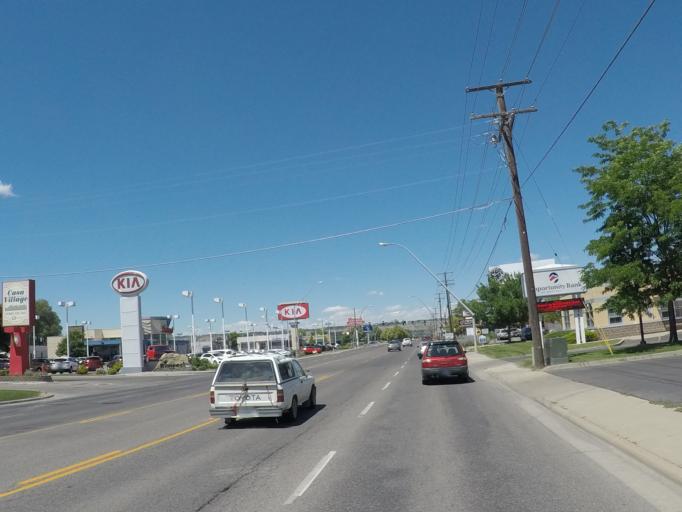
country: US
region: Montana
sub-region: Yellowstone County
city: Billings
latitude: 45.7610
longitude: -108.5761
